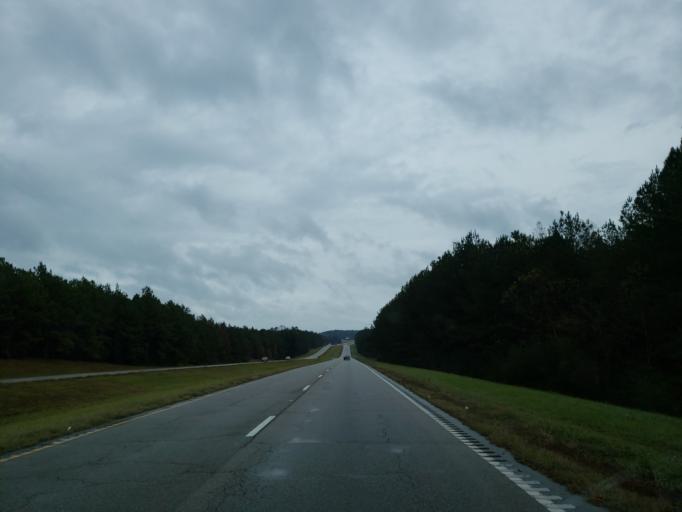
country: US
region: Mississippi
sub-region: Jones County
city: Laurel
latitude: 31.7021
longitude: -89.0876
